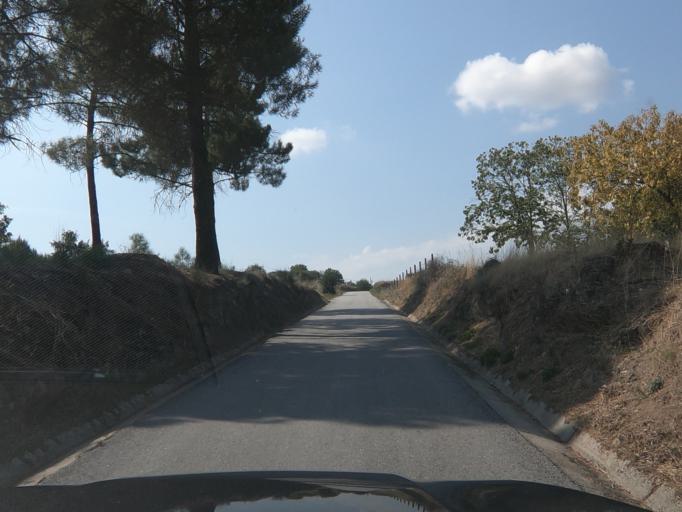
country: PT
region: Vila Real
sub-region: Sabrosa
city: Sabrosa
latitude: 41.3349
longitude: -7.6009
